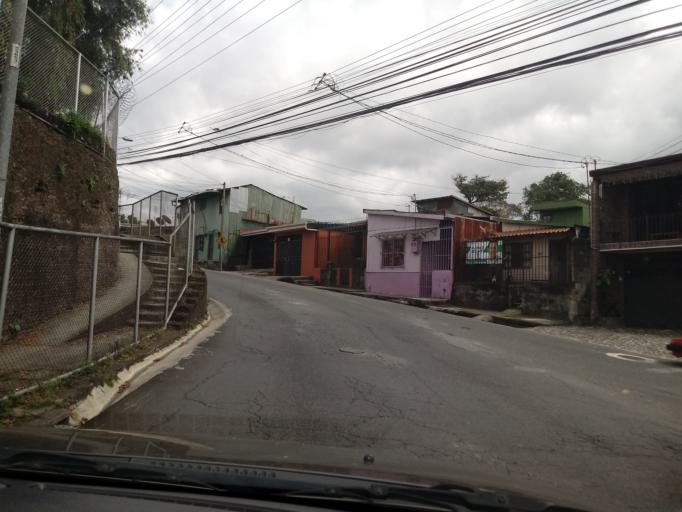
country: CR
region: San Jose
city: Calle Blancos
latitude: 9.9428
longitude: -84.0680
